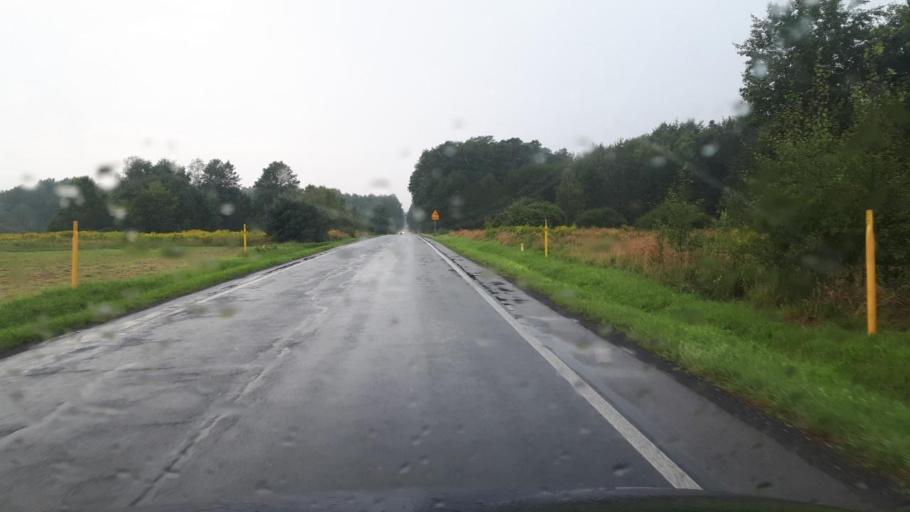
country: PL
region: Silesian Voivodeship
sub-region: Powiat tarnogorski
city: Tworog
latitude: 50.5312
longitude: 18.7069
